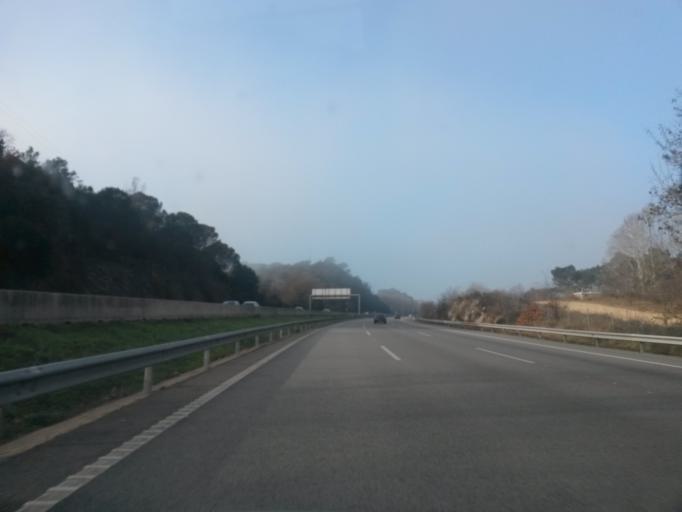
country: ES
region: Catalonia
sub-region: Provincia de Girona
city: Hostalric
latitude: 41.7297
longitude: 2.6299
